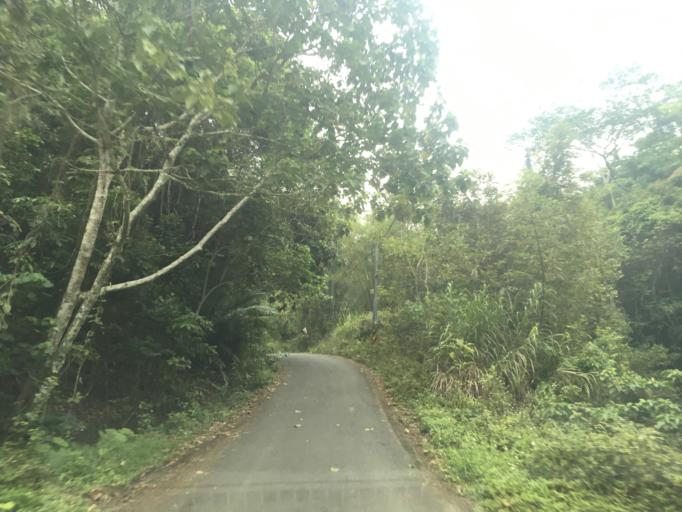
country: TW
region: Taiwan
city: Zhongxing New Village
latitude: 24.0481
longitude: 120.7845
